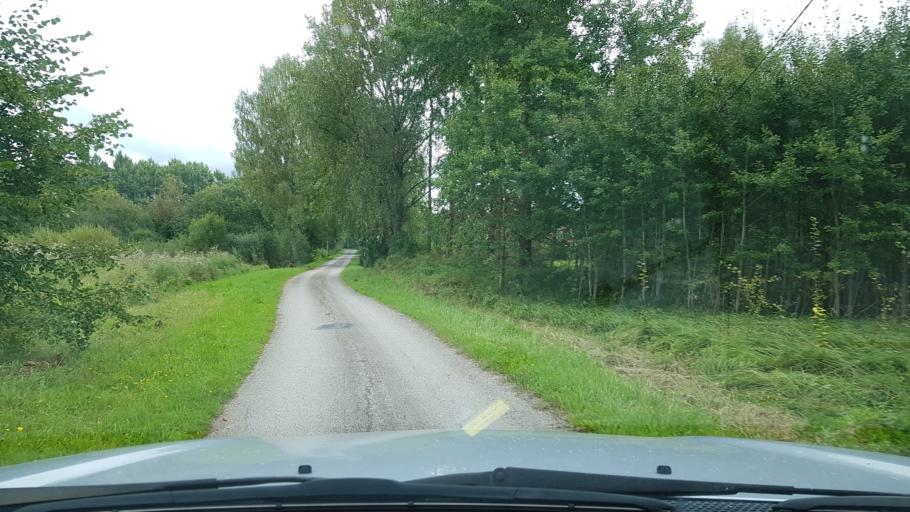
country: EE
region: Harju
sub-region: Raasiku vald
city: Arukula
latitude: 59.2902
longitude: 25.0727
